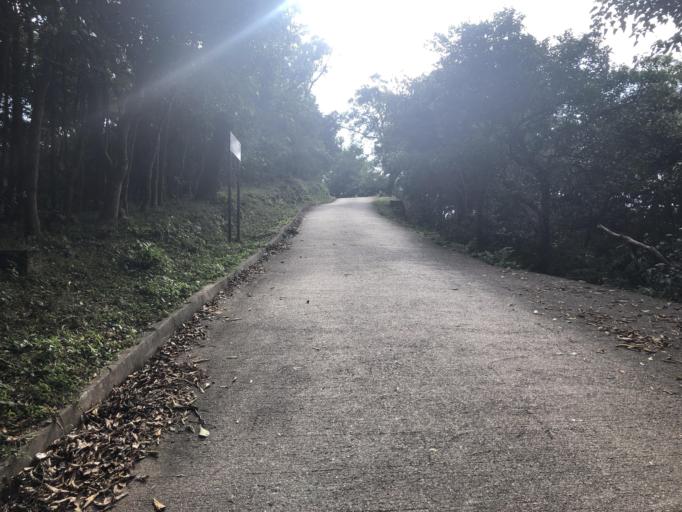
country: HK
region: Tsuen Wan
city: Tsuen Wan
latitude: 22.4018
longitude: 114.0956
